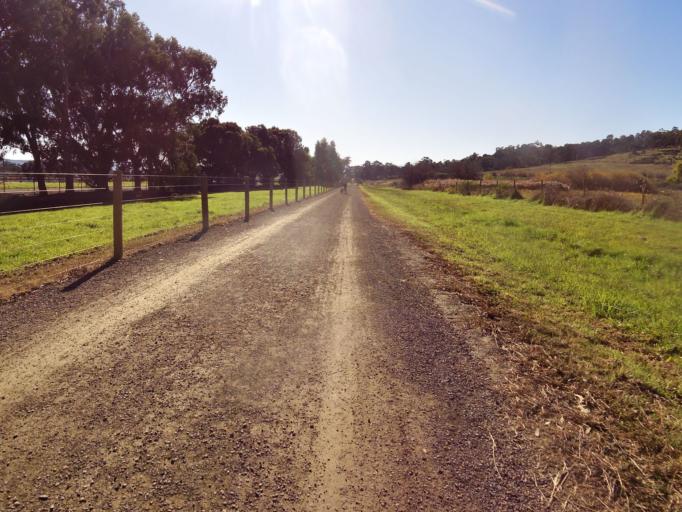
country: AU
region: Victoria
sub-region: Yarra Ranges
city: Lilydale
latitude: -37.7438
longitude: 145.3590
